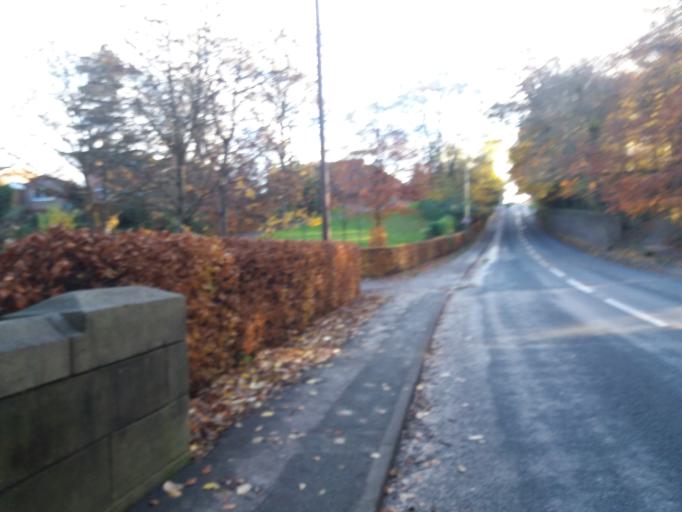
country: GB
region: England
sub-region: Lancashire
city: Euxton
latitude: 53.6644
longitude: -2.6748
